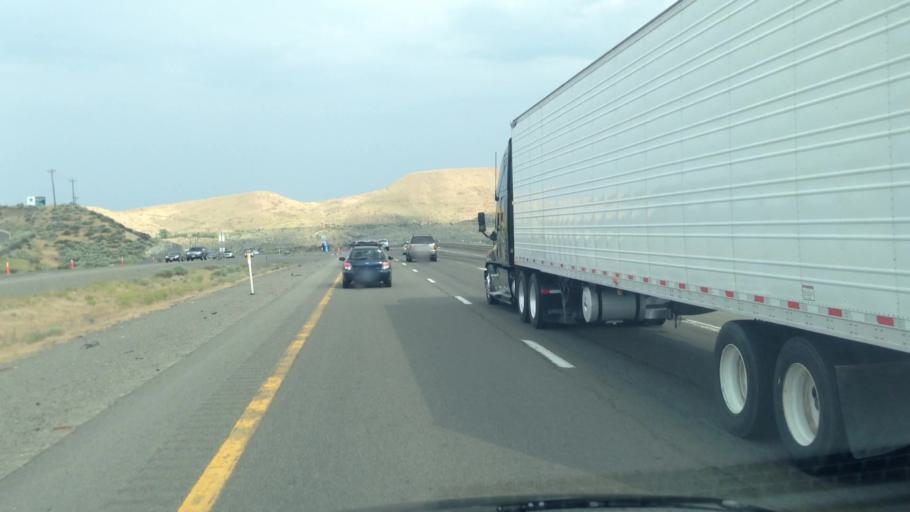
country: US
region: Nevada
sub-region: Washoe County
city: Mogul
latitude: 39.5111
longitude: -119.9456
